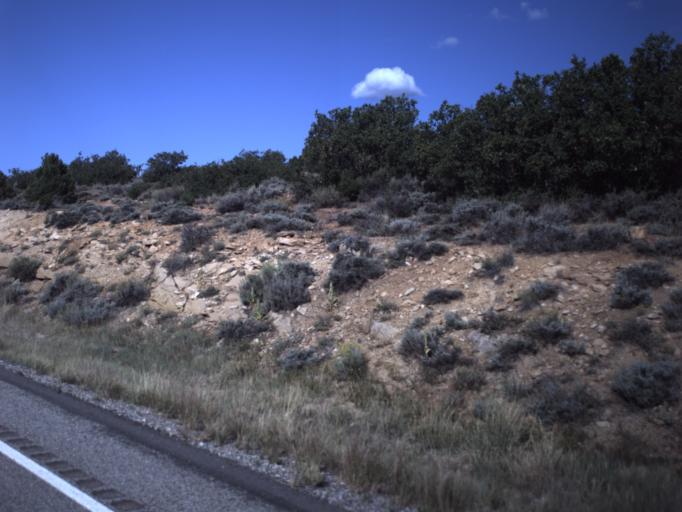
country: US
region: Utah
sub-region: San Juan County
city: Monticello
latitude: 37.7633
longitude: -109.3888
